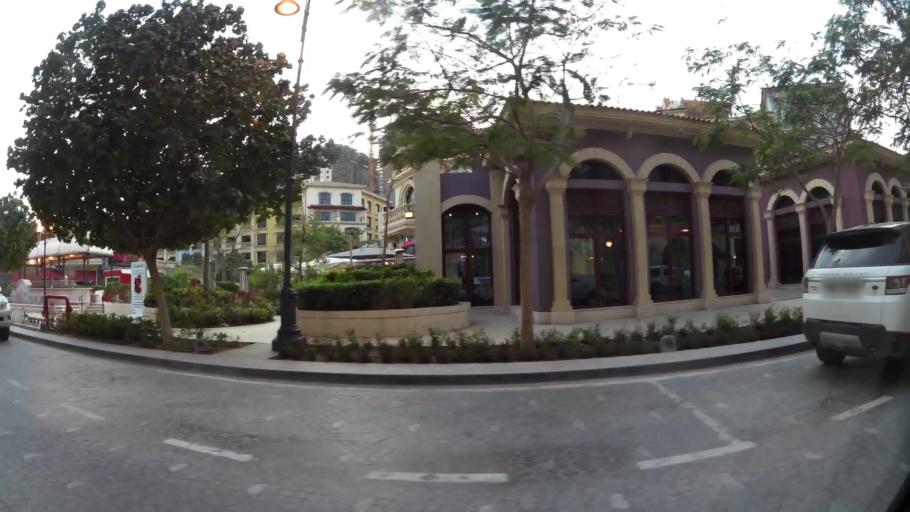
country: QA
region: Baladiyat ad Dawhah
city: Doha
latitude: 25.3686
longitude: 51.5515
